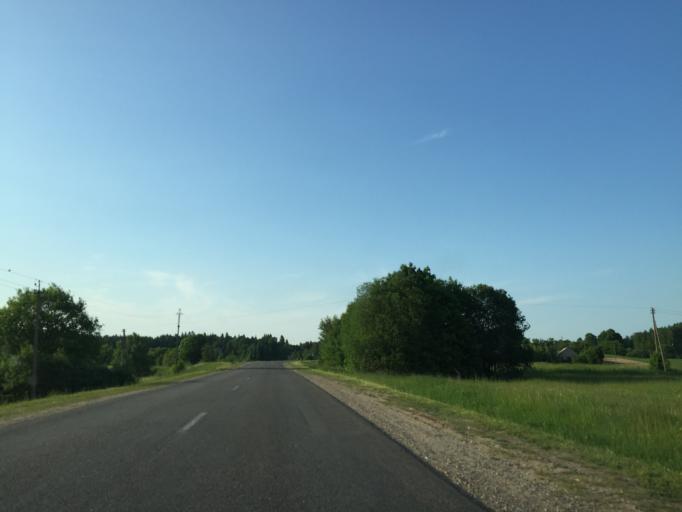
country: LT
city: Plateliai
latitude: 56.0575
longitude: 21.8197
